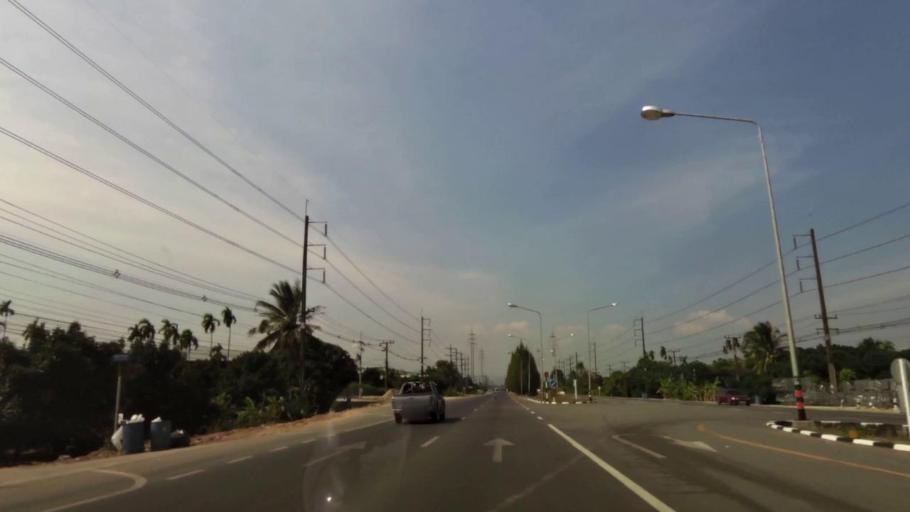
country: TH
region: Chanthaburi
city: Chanthaburi
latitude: 12.6340
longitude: 102.1406
